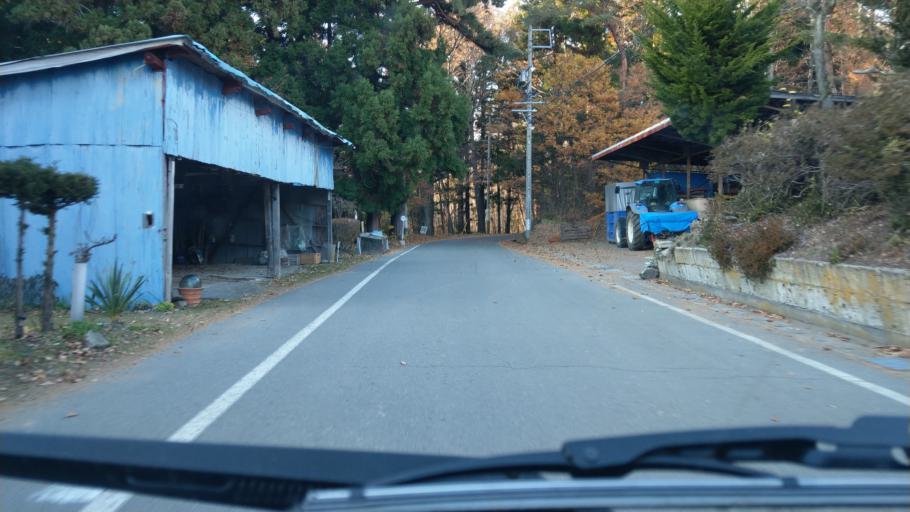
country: JP
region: Nagano
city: Komoro
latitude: 36.3550
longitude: 138.4556
